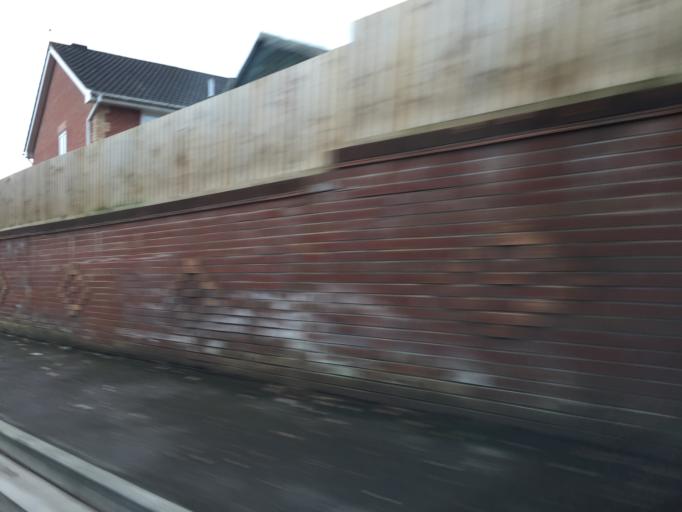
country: GB
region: Wales
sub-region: Monmouthshire
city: Chepstow
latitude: 51.6249
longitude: -2.6646
